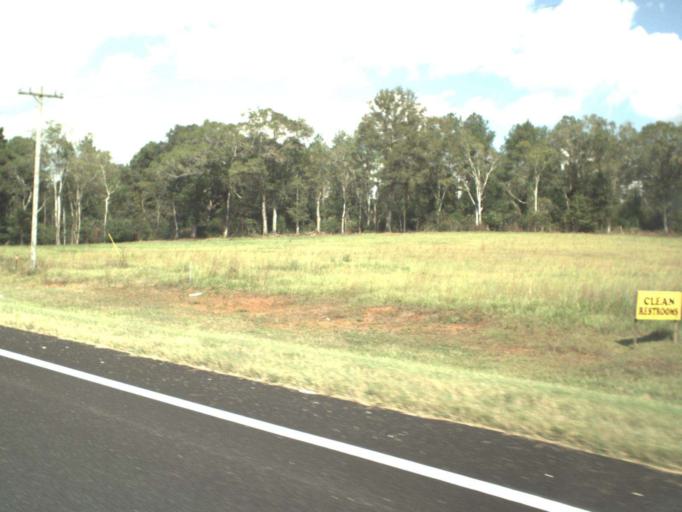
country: US
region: Florida
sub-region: Jackson County
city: Marianna
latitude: 30.8457
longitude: -85.3468
